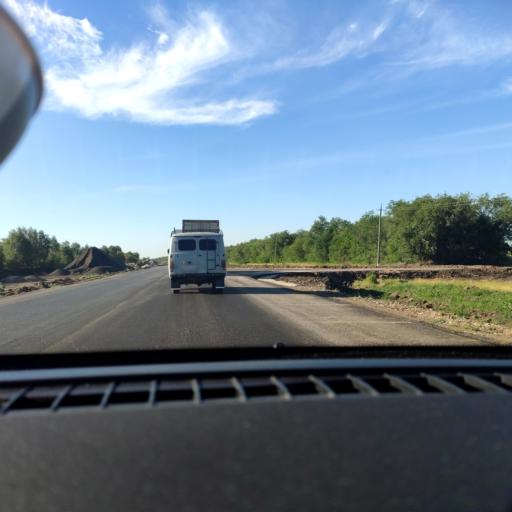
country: RU
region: Samara
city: Krasnoarmeyskoye
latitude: 52.8290
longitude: 50.0073
